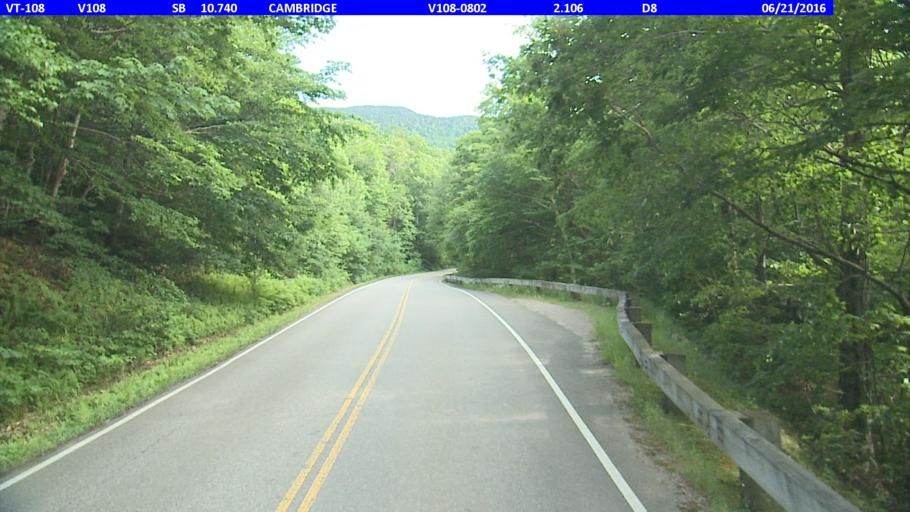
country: US
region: Vermont
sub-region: Lamoille County
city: Johnson
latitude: 44.5671
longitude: -72.7839
